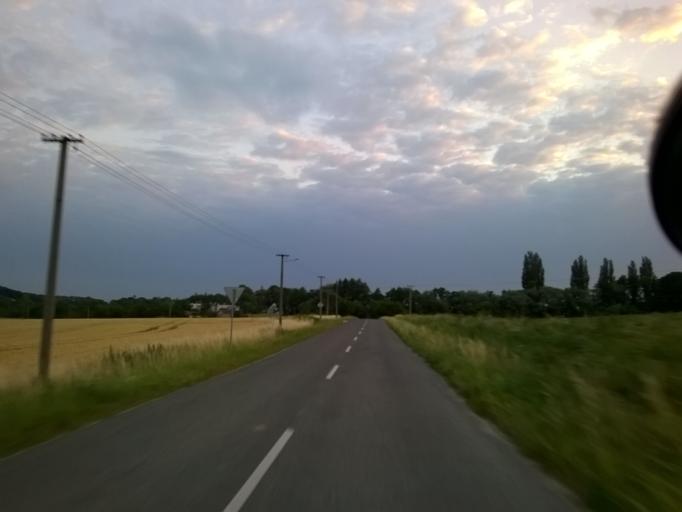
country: SK
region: Trnavsky
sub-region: Okres Senica
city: Senica
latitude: 48.7320
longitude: 17.3540
